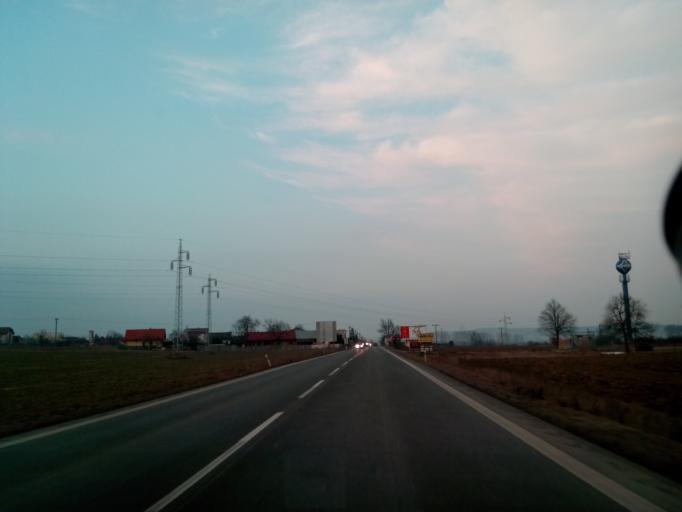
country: SK
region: Kosicky
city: Kosice
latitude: 48.6492
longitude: 21.2695
